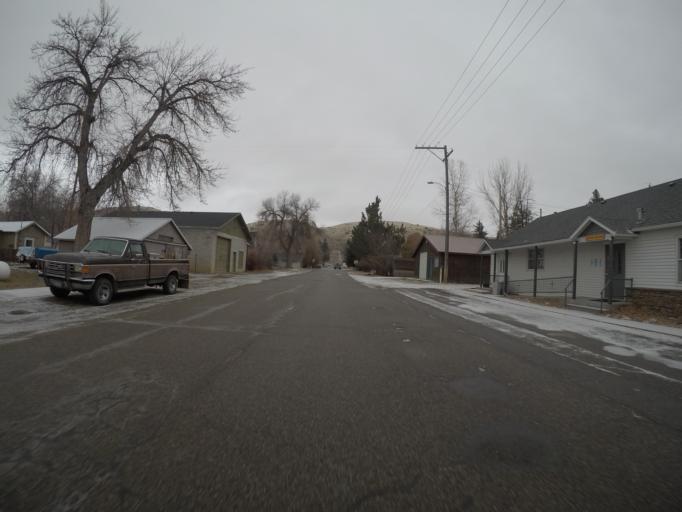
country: US
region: Montana
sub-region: Stillwater County
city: Absarokee
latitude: 45.5189
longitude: -109.4435
